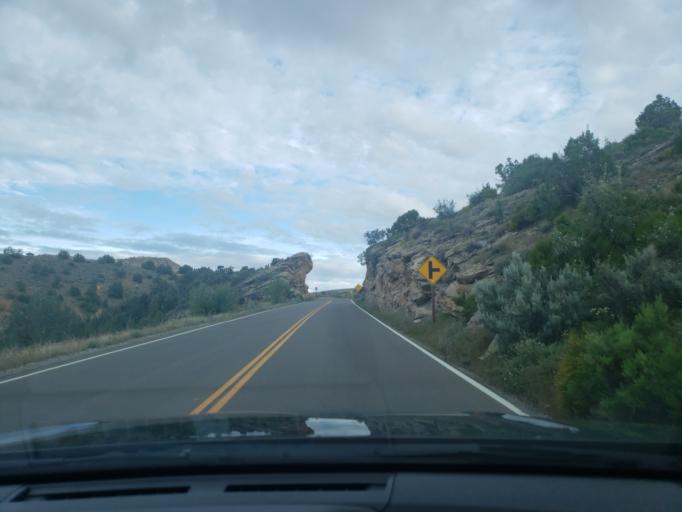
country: US
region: Colorado
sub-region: Mesa County
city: Redlands
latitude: 39.0332
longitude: -108.6317
